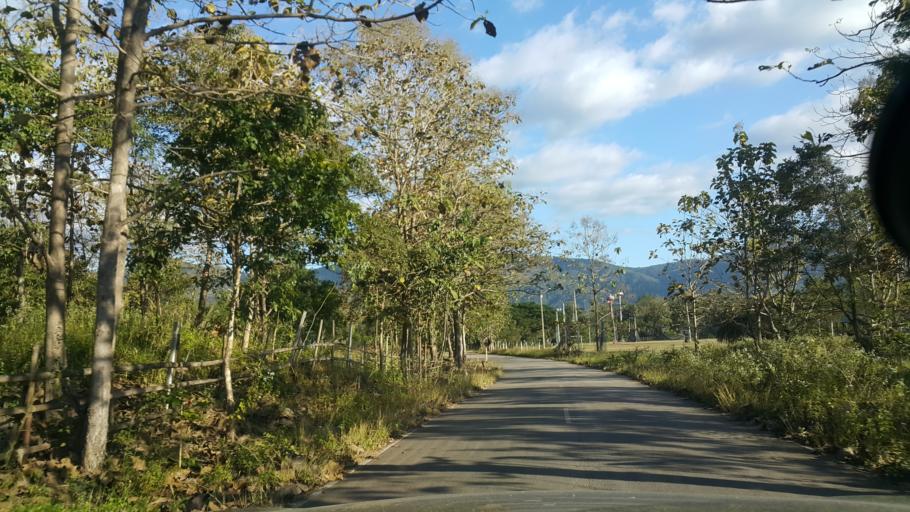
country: TH
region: Chiang Mai
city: Mae On
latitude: 18.7733
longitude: 99.2488
